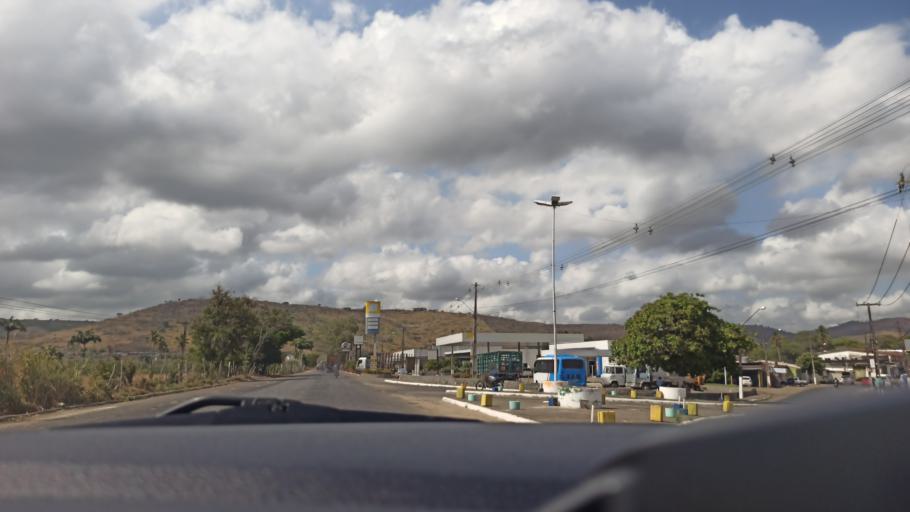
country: BR
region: Pernambuco
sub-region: Timbauba
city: Timbauba
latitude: -7.5129
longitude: -35.3031
